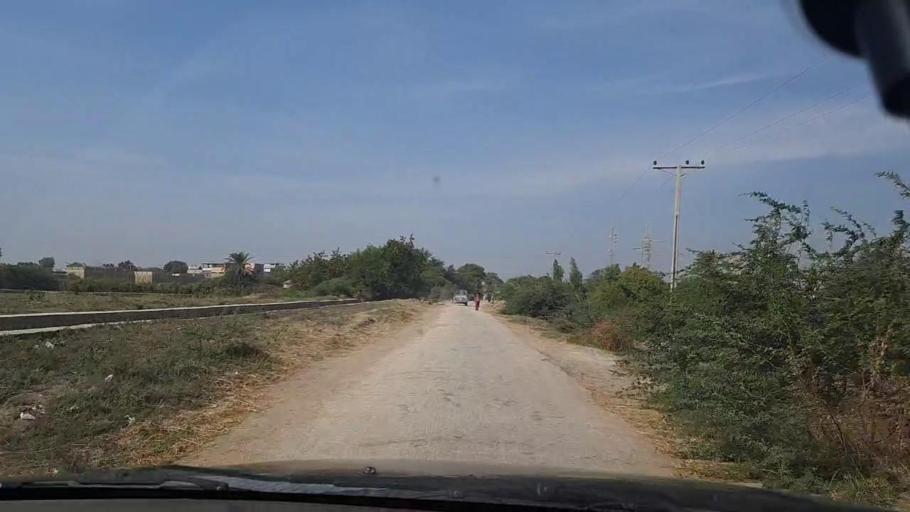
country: PK
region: Sindh
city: Mirpur Batoro
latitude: 24.7336
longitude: 68.2586
